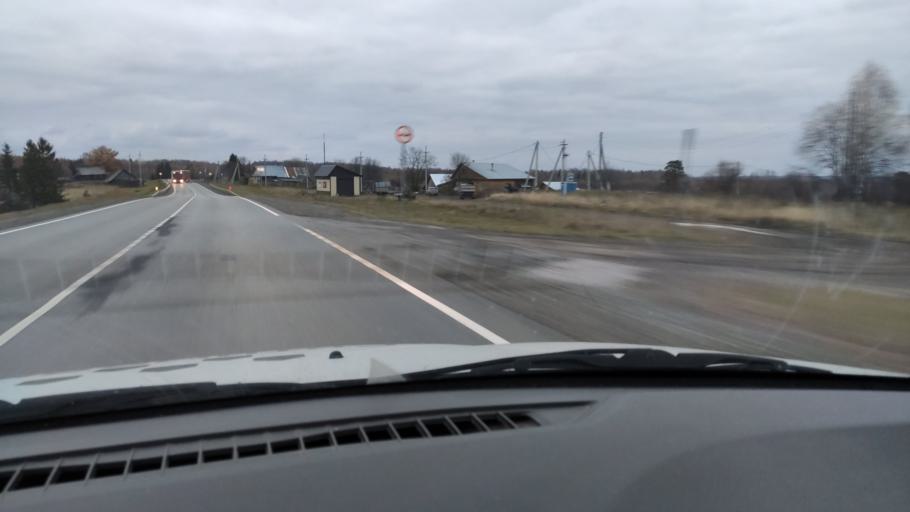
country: RU
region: Kirov
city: Kostino
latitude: 58.7958
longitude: 52.8883
